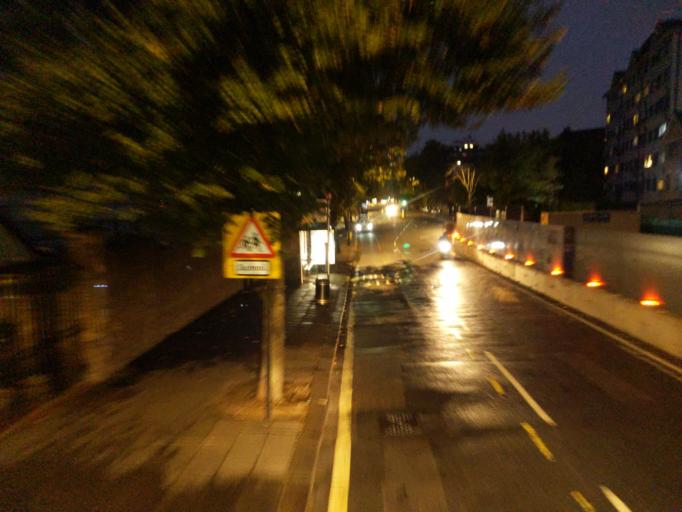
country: GB
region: England
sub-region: Greater London
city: Bayswater
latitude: 51.5255
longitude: -0.1700
